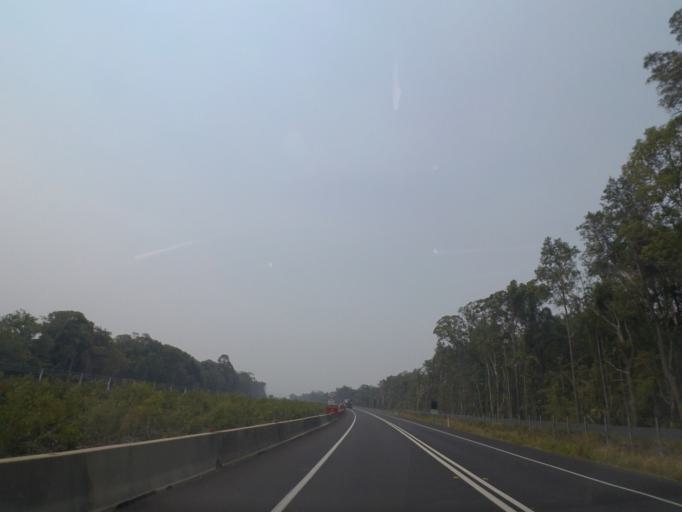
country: AU
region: New South Wales
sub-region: Ballina
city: Ballina
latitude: -28.9150
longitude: 153.4779
